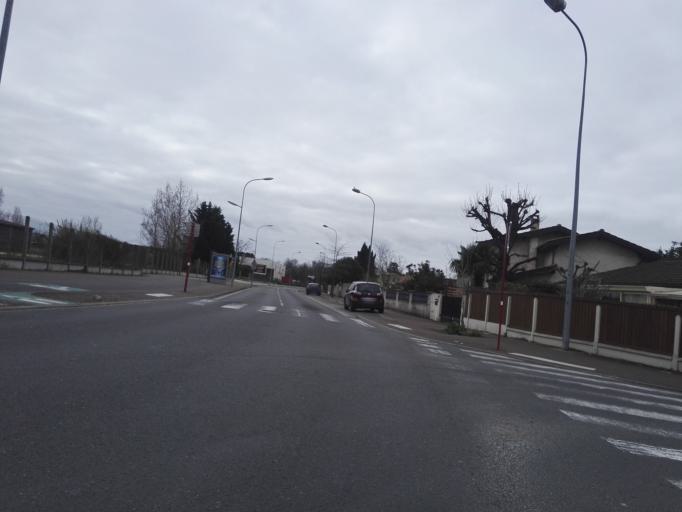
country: FR
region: Aquitaine
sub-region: Departement de la Gironde
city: Talence
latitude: 44.7952
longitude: -0.5805
